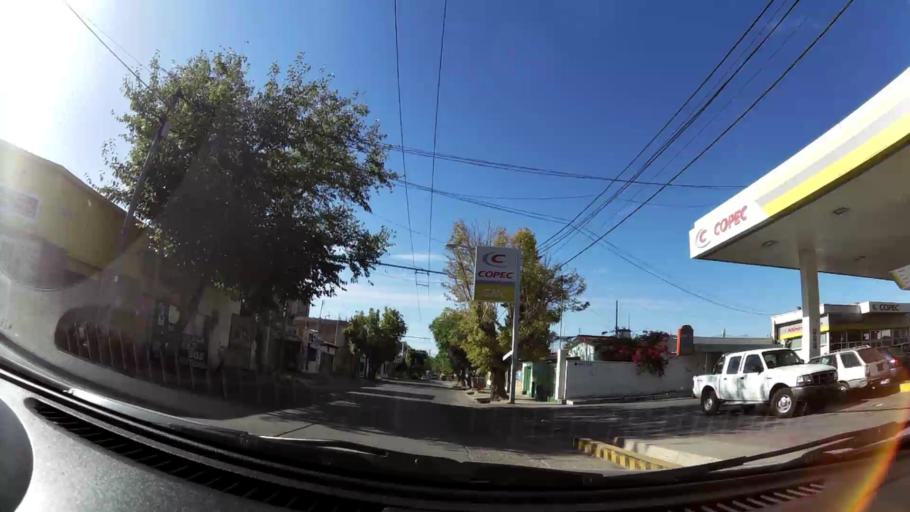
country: AR
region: Mendoza
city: Mendoza
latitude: -32.9050
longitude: -68.8308
